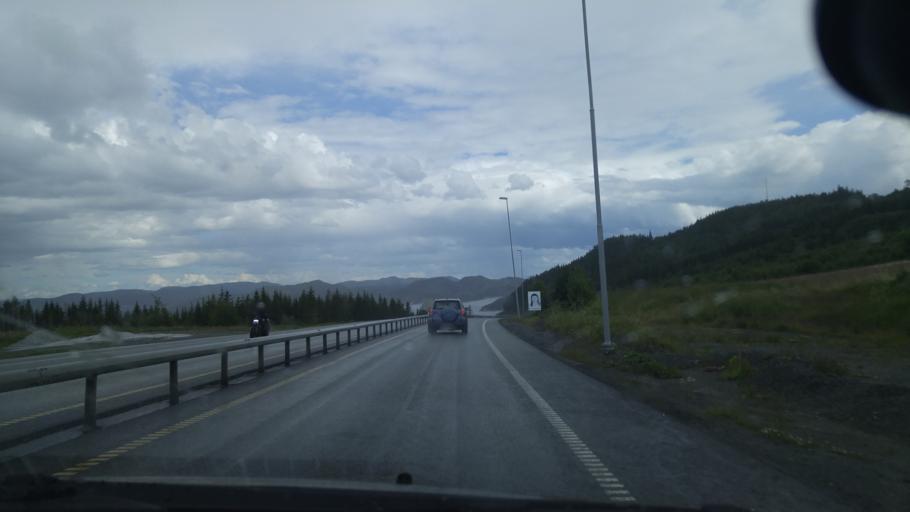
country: NO
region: Nord-Trondelag
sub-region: Stjordal
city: Stjordal
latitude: 63.5321
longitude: 10.8375
